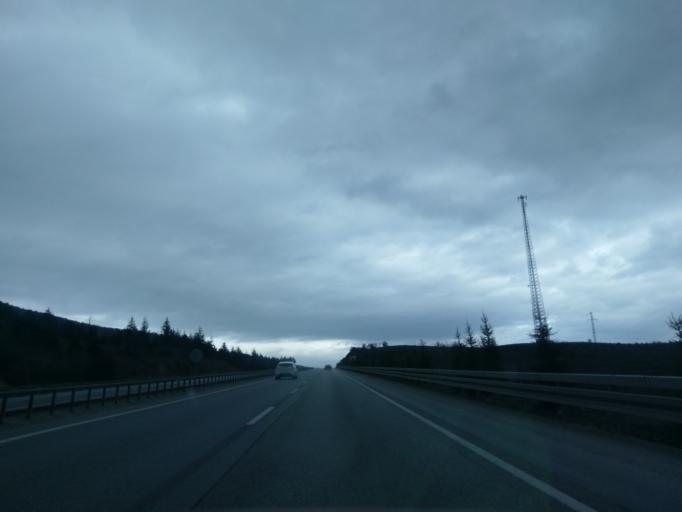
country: TR
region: Kuetahya
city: Sabuncu
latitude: 39.5753
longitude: 30.1182
